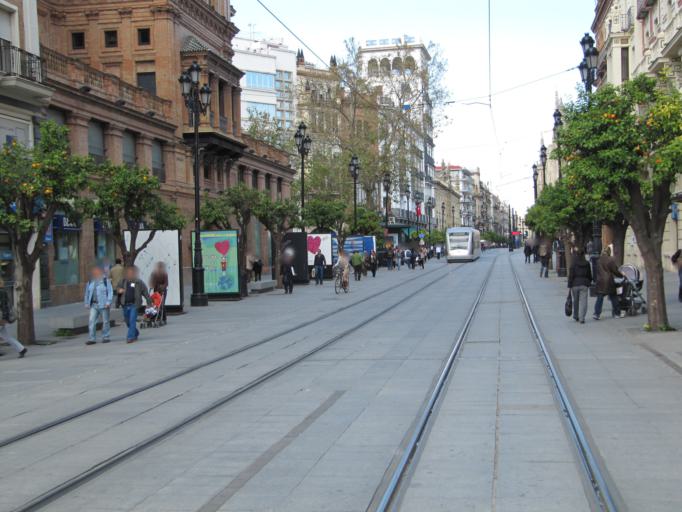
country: ES
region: Andalusia
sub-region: Provincia de Sevilla
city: Sevilla
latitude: 37.3832
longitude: -5.9936
